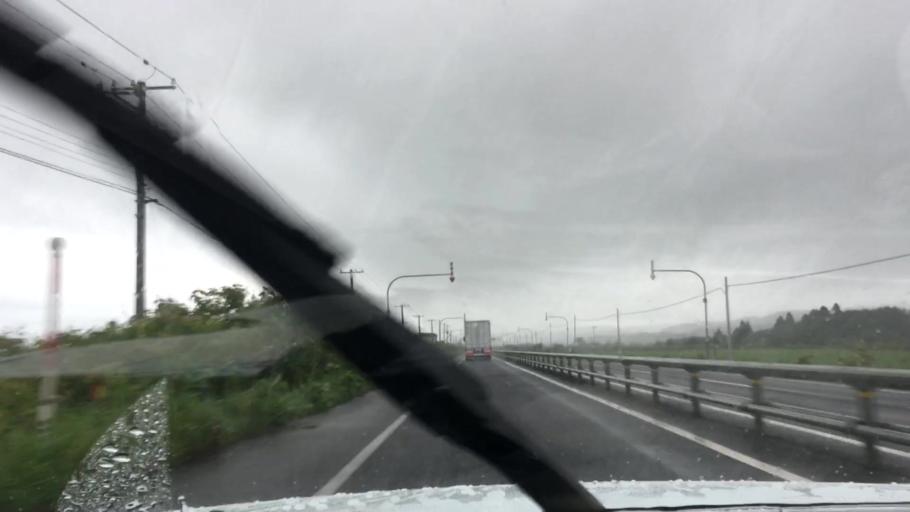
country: JP
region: Hokkaido
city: Niseko Town
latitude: 42.4166
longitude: 140.3105
